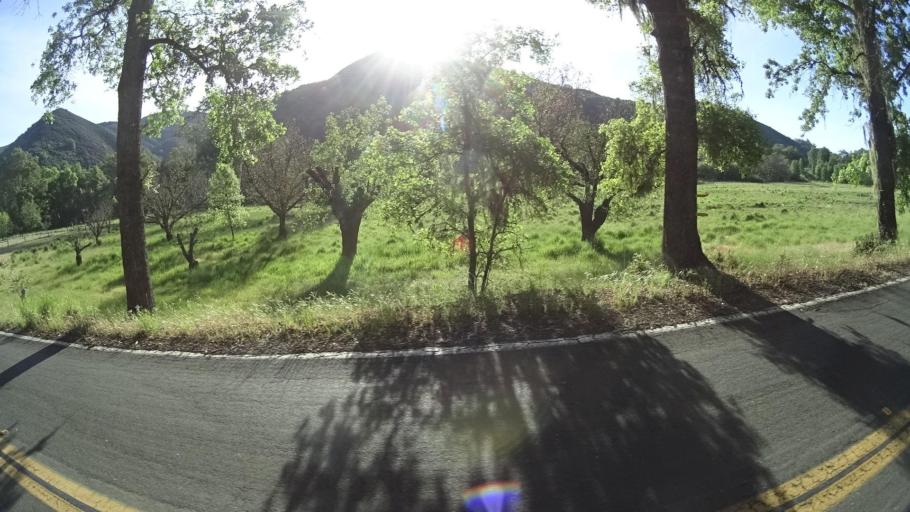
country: US
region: California
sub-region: Lake County
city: Upper Lake
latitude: 39.1329
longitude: -122.9981
